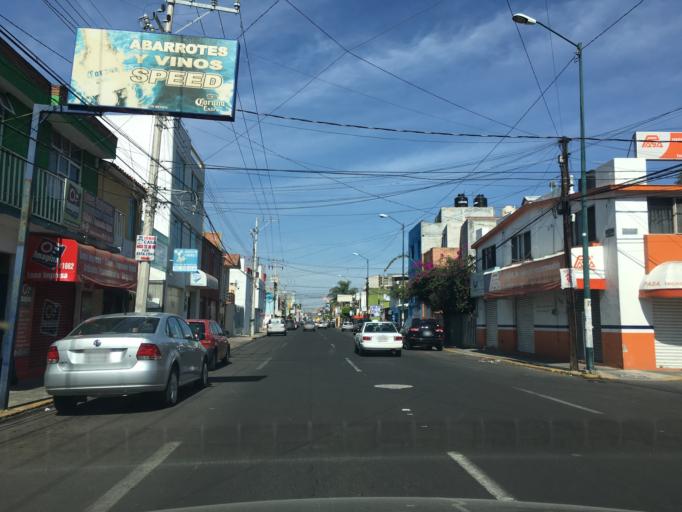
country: MX
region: Michoacan
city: Morelia
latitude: 19.6858
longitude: -101.1907
